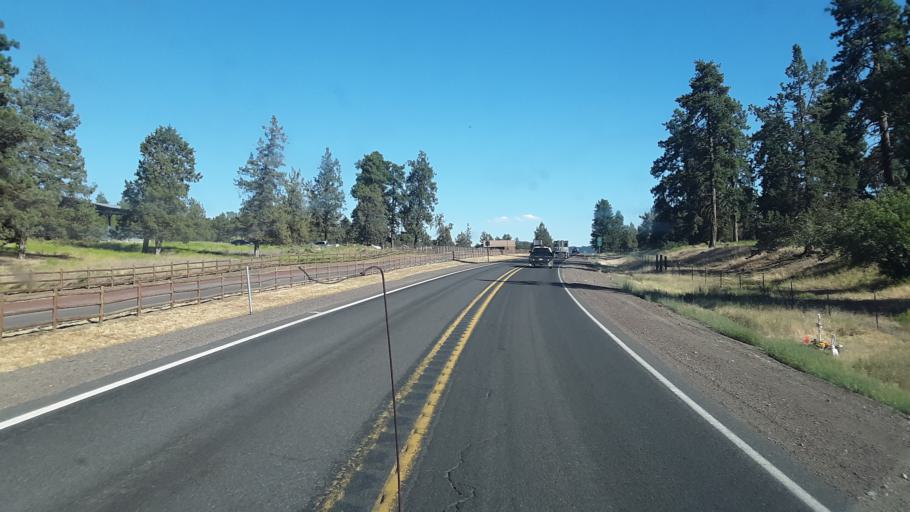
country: US
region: Oregon
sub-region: Klamath County
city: Klamath Falls
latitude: 42.2696
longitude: -121.8803
